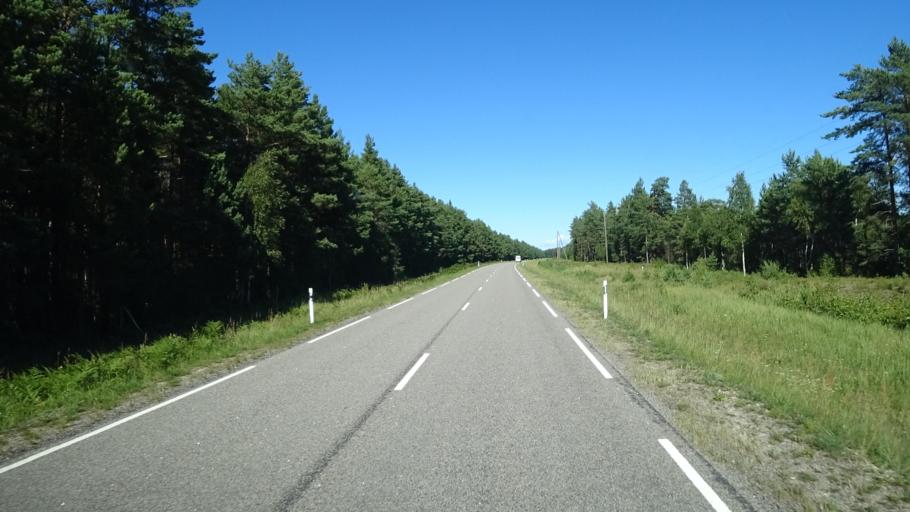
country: LV
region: Dundaga
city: Dundaga
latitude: 57.7151
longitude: 22.4602
